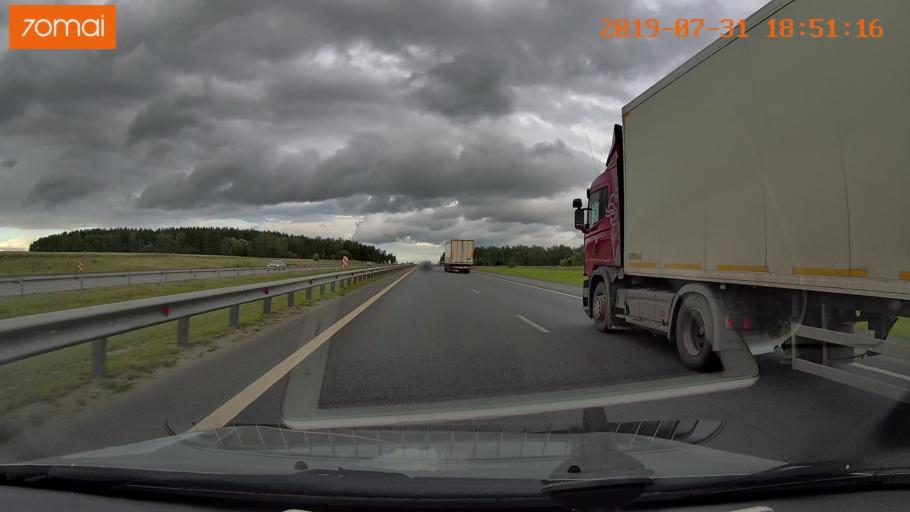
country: RU
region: Moskovskaya
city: Troitskoye
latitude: 55.2227
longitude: 38.6028
